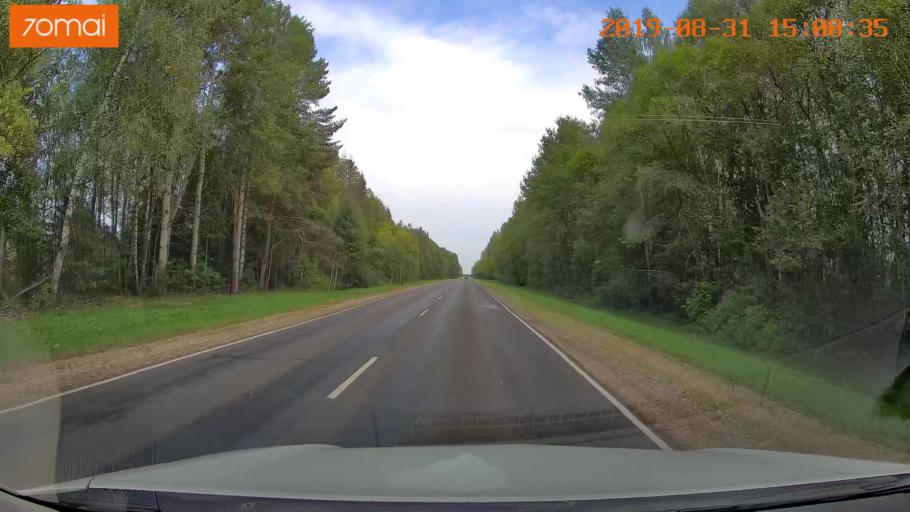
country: RU
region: Kaluga
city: Spas-Demensk
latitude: 54.3332
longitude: 34.0353
